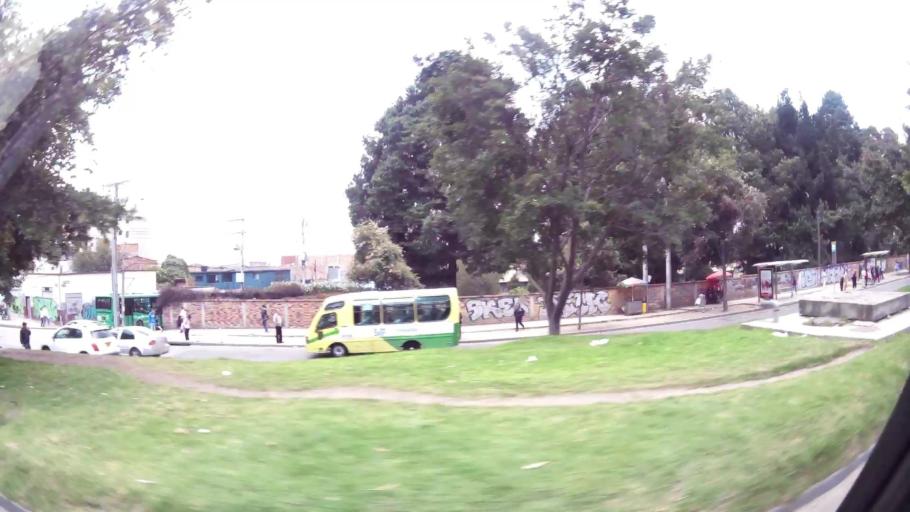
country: CO
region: Cundinamarca
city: La Calera
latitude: 4.7386
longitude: -74.0227
